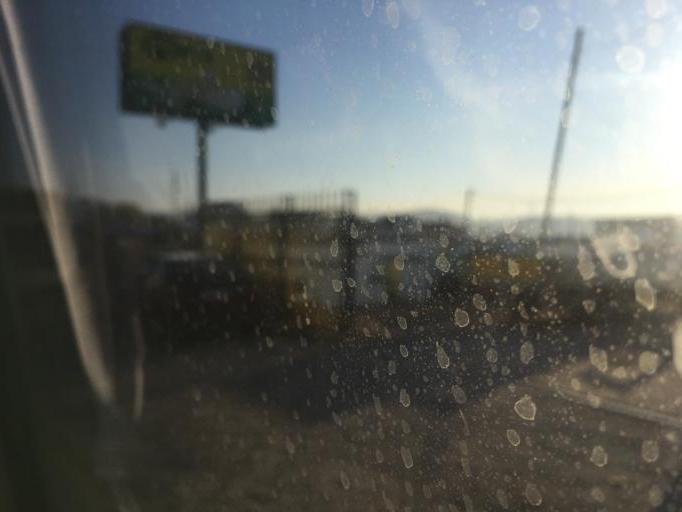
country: XK
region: Pristina
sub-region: Komuna e Drenasit
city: Glogovac
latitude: 42.6258
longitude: 20.8989
